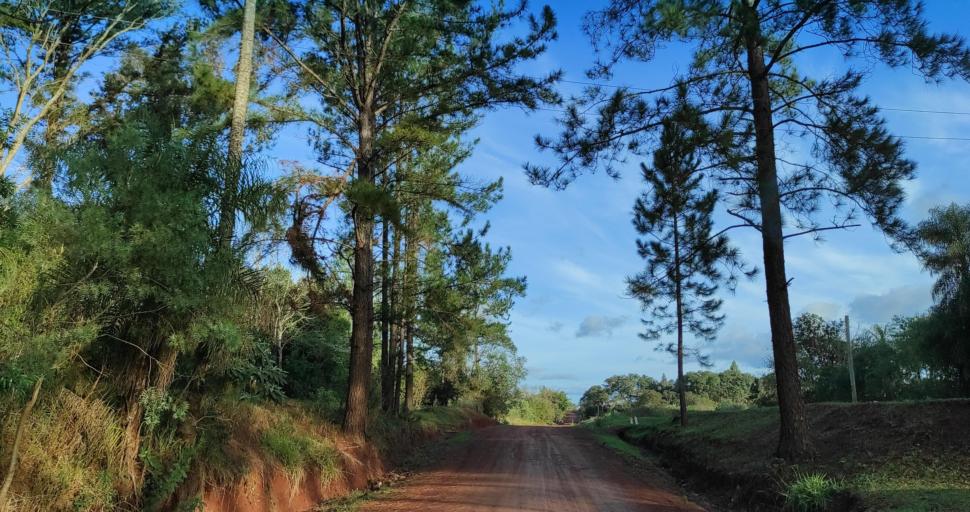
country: AR
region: Misiones
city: Garupa
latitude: -27.5138
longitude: -55.8540
